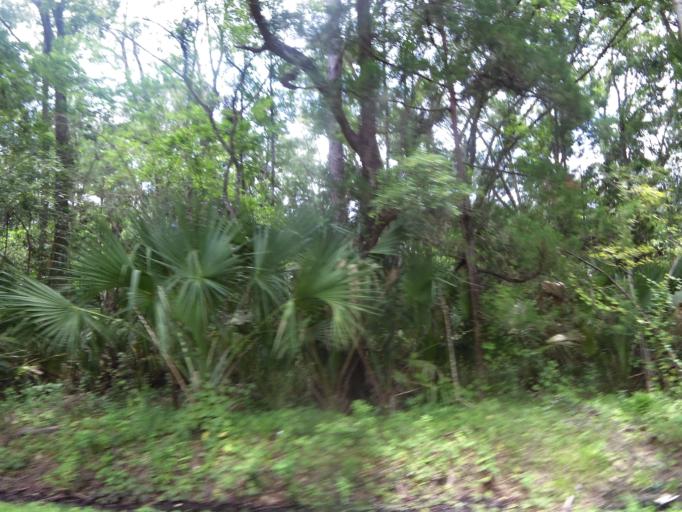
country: US
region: Florida
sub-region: Putnam County
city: East Palatka
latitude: 29.7156
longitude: -81.5069
